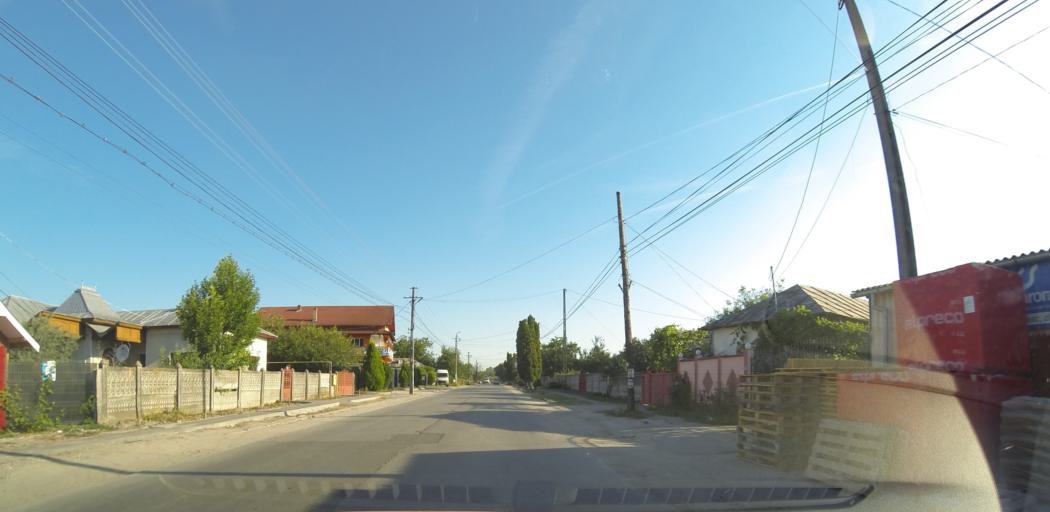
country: RO
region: Valcea
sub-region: Comuna Balcesti
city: Balcesti
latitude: 44.6248
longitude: 23.9416
